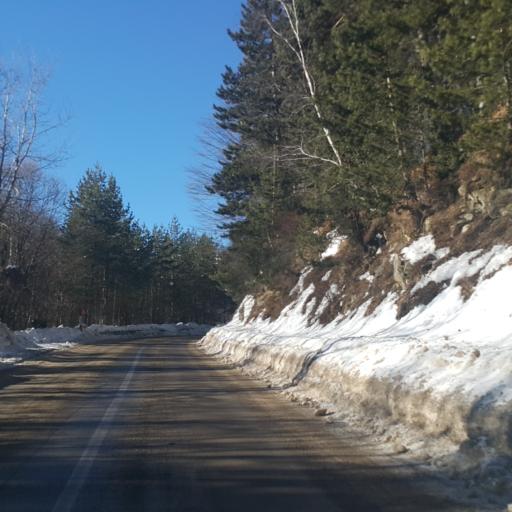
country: XK
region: Mitrovica
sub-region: Komuna e Leposaviqit
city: Leposaviq
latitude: 43.3108
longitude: 20.8632
